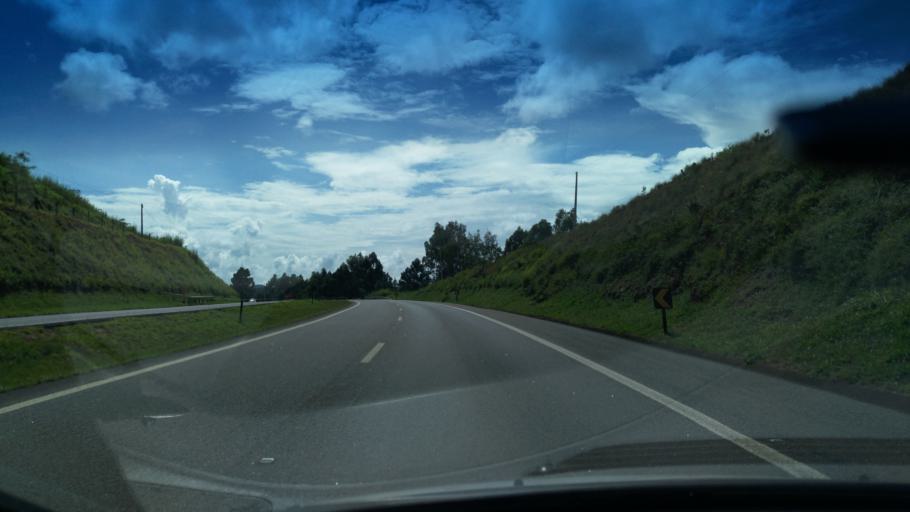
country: BR
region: Sao Paulo
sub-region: Santo Antonio Do Jardim
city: Espirito Santo do Pinhal
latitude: -22.2078
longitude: -46.7792
